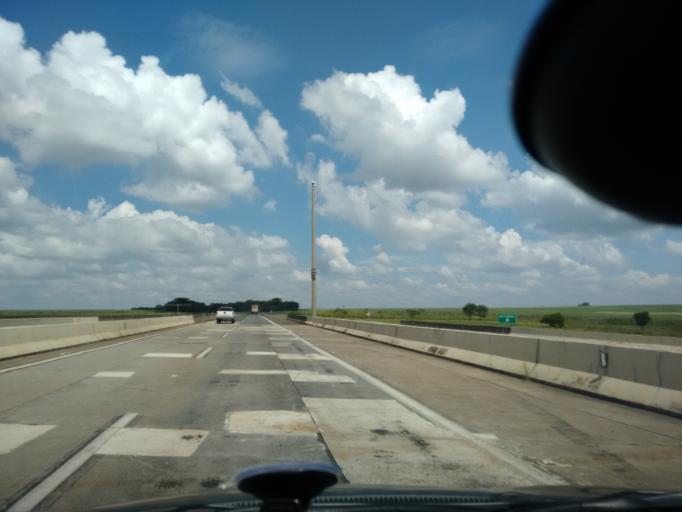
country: BR
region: Sao Paulo
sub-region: Santa Barbara D'Oeste
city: Santa Barbara d'Oeste
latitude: -22.7654
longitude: -47.4458
